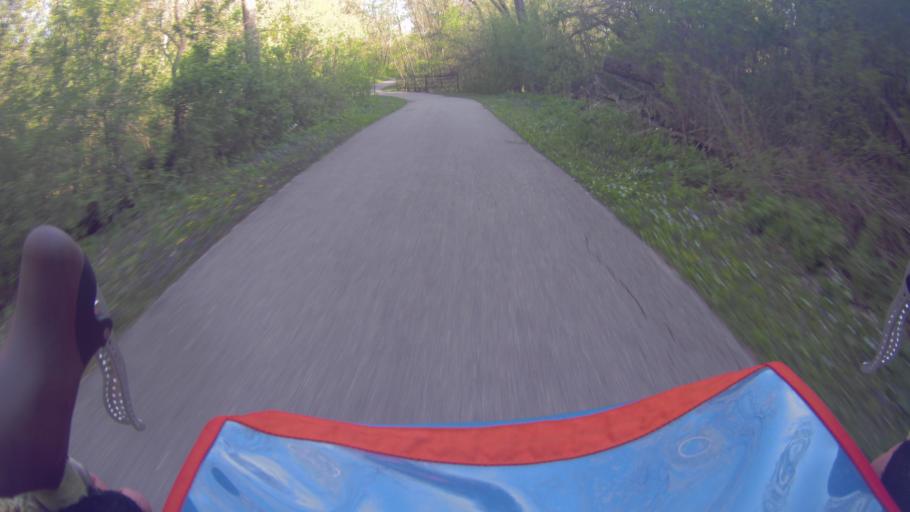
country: US
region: Wisconsin
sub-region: Dane County
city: Madison
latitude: 43.0196
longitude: -89.4264
